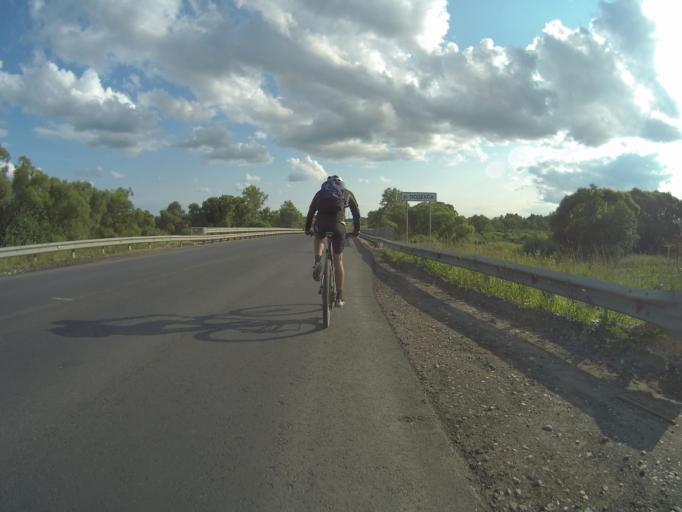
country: RU
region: Vladimir
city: Kideksha
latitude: 56.5121
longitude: 40.5489
